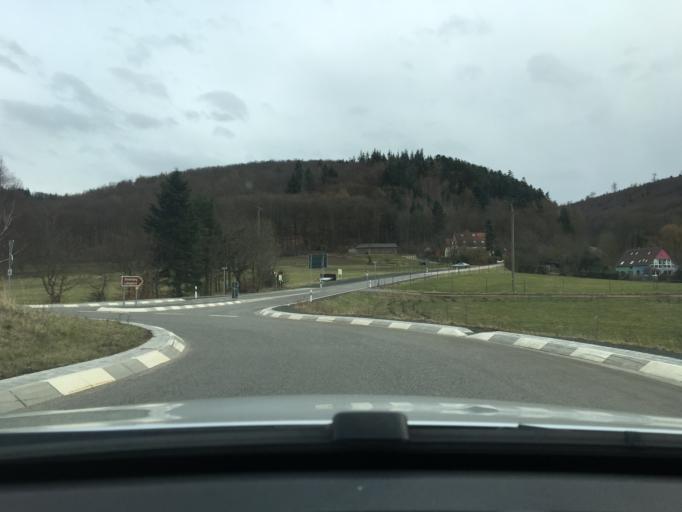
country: DE
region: Rheinland-Pfalz
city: Dannenfels
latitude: 49.6407
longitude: 7.9172
